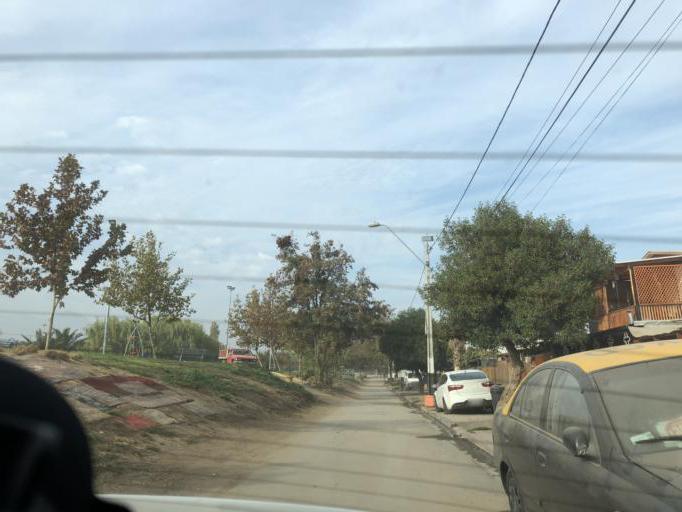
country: CL
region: Santiago Metropolitan
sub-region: Provincia de Cordillera
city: Puente Alto
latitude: -33.5616
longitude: -70.5532
